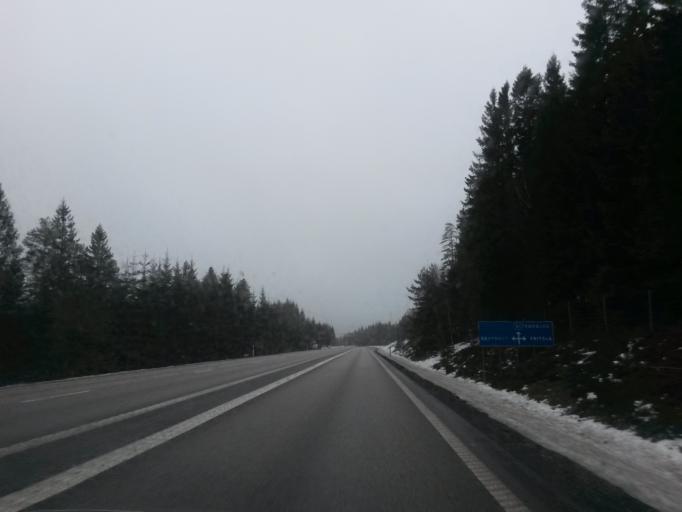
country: SE
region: Vaestra Goetaland
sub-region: Marks Kommun
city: Fritsla
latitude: 57.5409
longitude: 12.8088
